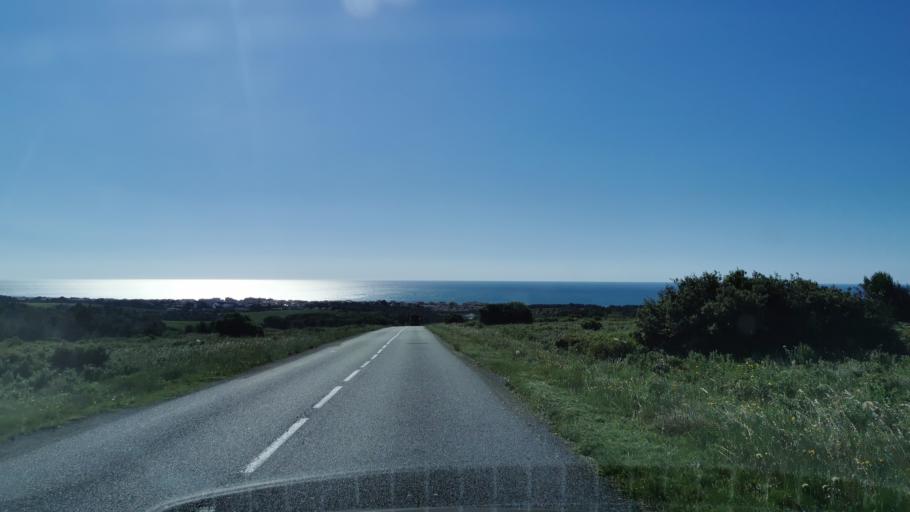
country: FR
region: Languedoc-Roussillon
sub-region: Departement de l'Aude
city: Armissan
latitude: 43.1610
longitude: 3.1387
